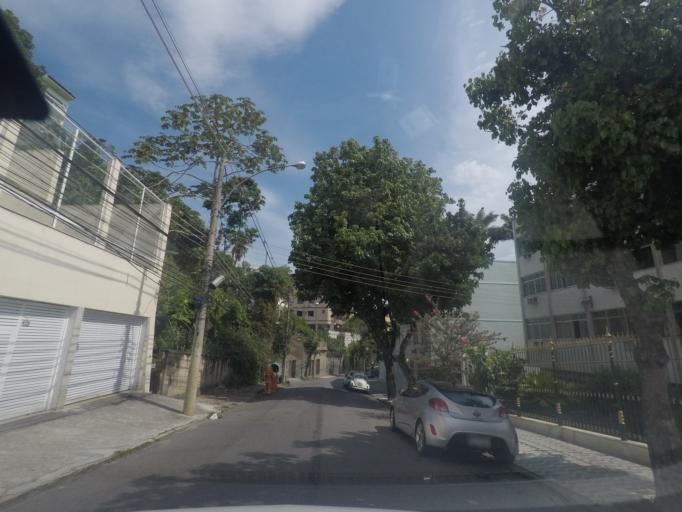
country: BR
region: Rio de Janeiro
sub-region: Rio De Janeiro
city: Rio de Janeiro
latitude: -22.8155
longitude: -43.1959
